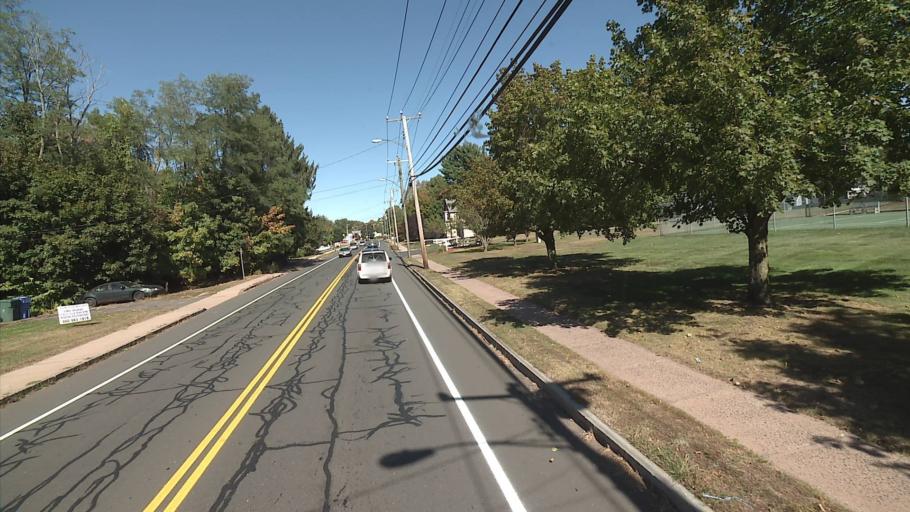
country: US
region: Connecticut
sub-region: Hartford County
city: Manchester
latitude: 41.8003
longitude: -72.5194
